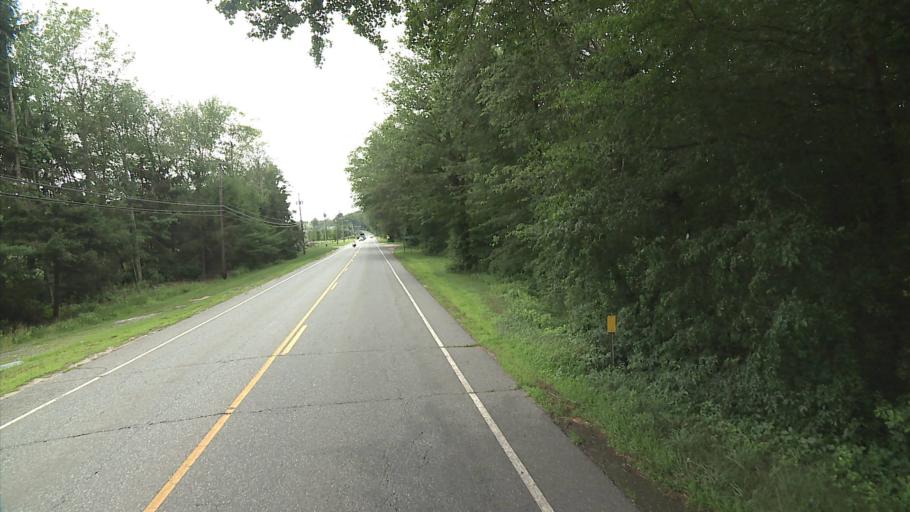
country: US
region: Connecticut
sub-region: Middlesex County
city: Deep River Center
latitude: 41.3681
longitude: -72.4598
